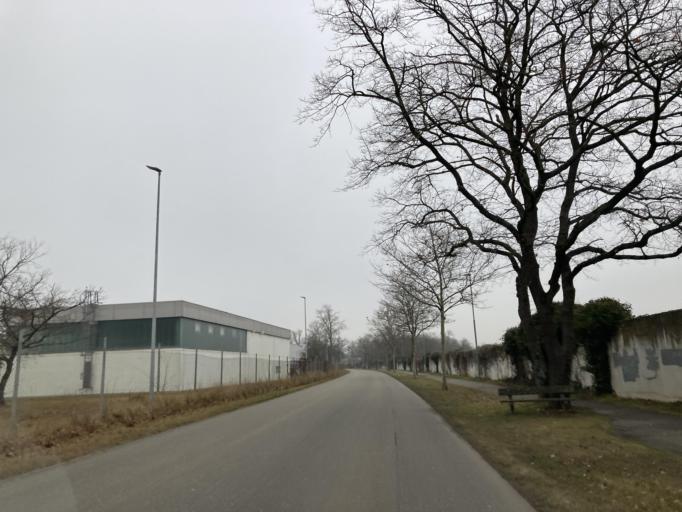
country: DE
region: Baden-Wuerttemberg
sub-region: Freiburg Region
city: Neuenburg am Rhein
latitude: 47.8012
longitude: 7.5536
